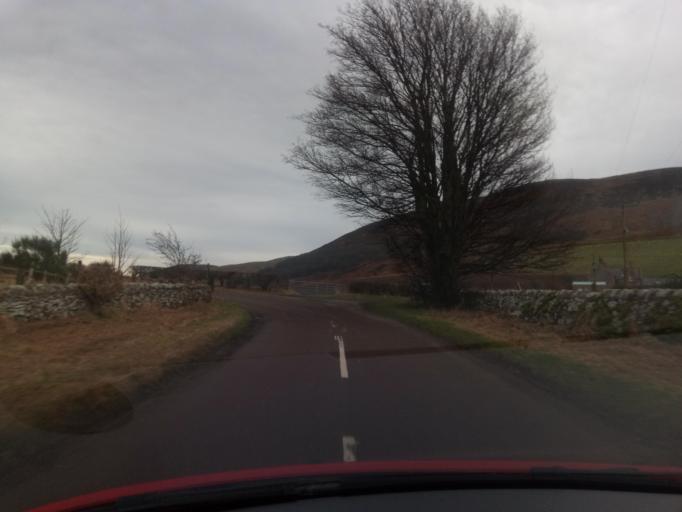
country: GB
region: England
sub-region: Northumberland
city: Kirknewton
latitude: 55.5675
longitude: -2.1228
